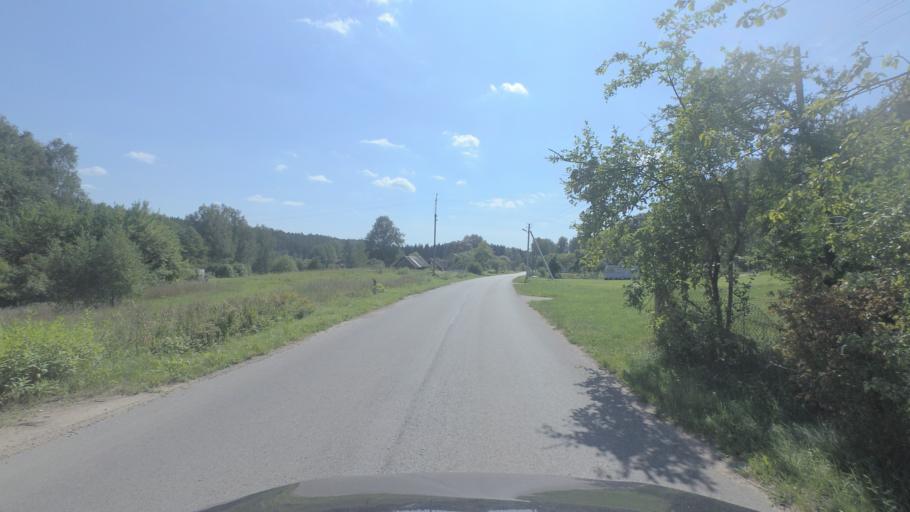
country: LT
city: Nemencine
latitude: 54.8476
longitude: 25.3736
